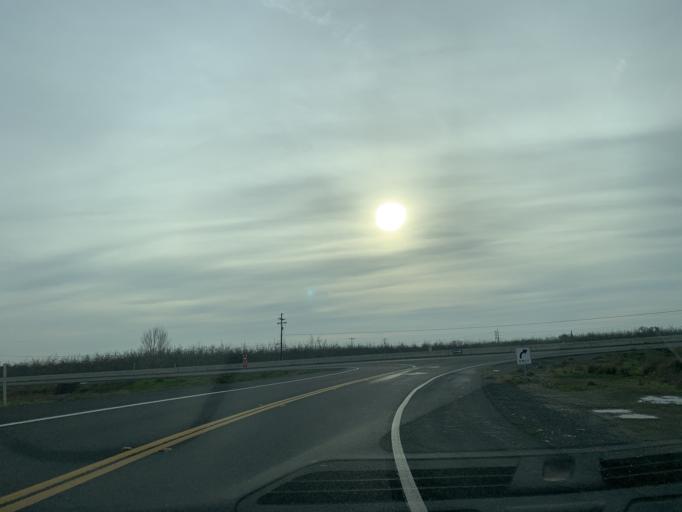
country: US
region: California
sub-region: Yuba County
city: Plumas Lake
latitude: 38.8974
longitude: -121.5804
